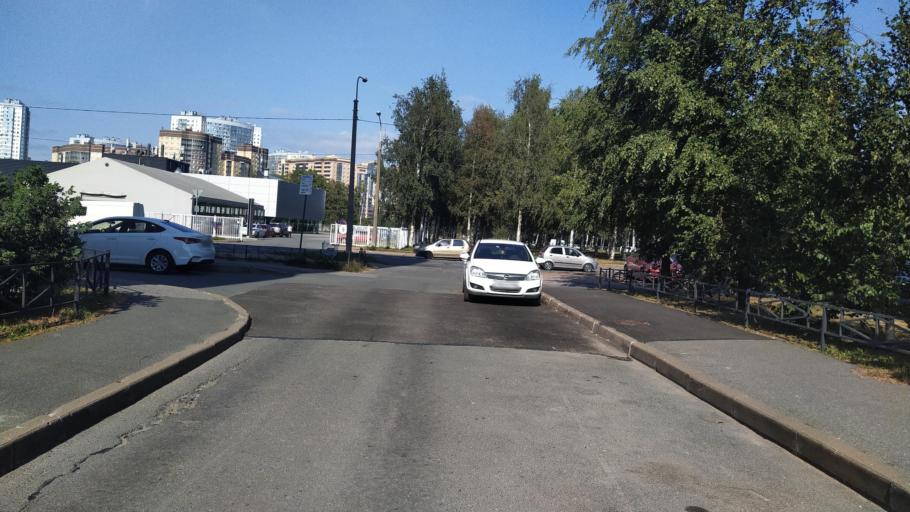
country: RU
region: Leningrad
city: Untolovo
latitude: 59.9912
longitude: 30.2152
